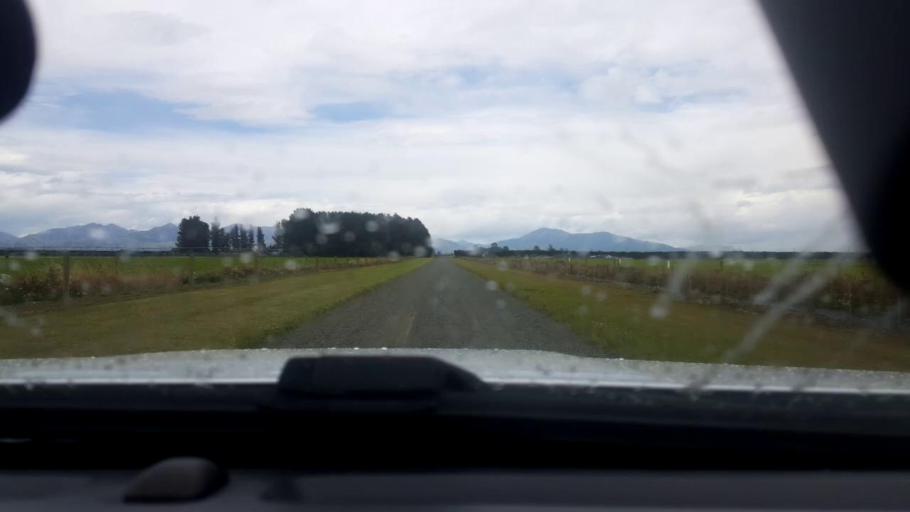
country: NZ
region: Canterbury
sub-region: Timaru District
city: Pleasant Point
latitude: -44.1121
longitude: 171.3525
